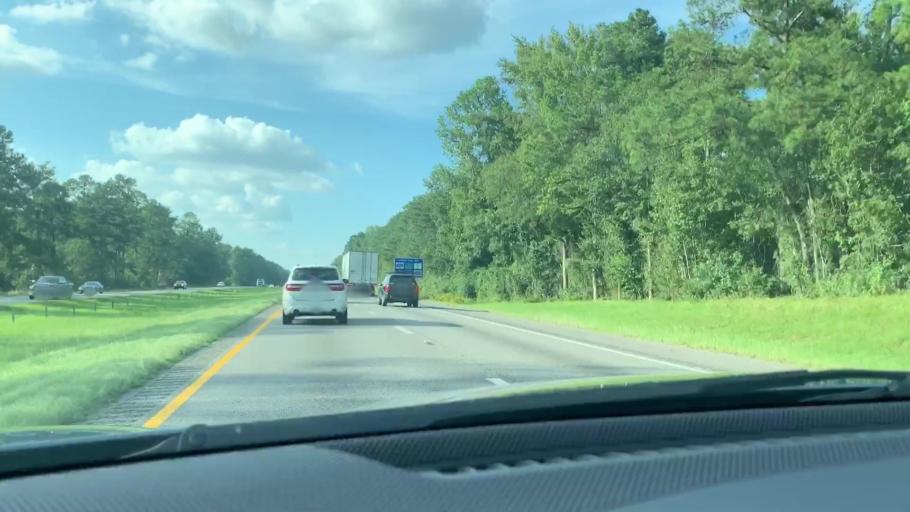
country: US
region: South Carolina
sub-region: Orangeburg County
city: Brookdale
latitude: 33.5427
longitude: -80.8106
